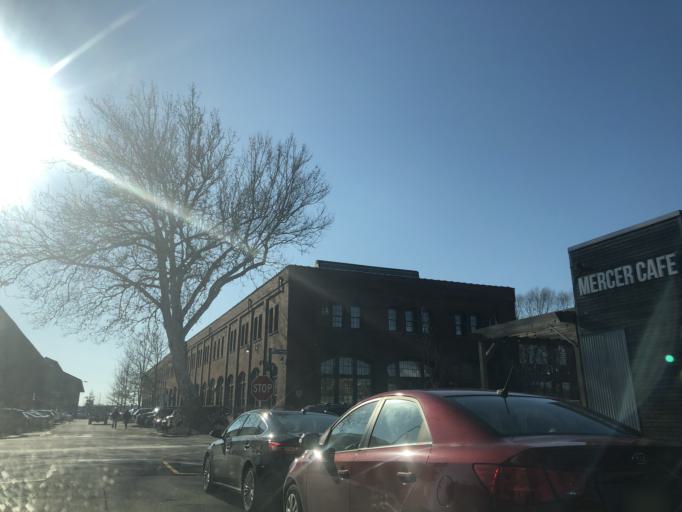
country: US
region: New Jersey
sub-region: Gloucester County
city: National Park
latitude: 39.8902
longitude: -75.1771
